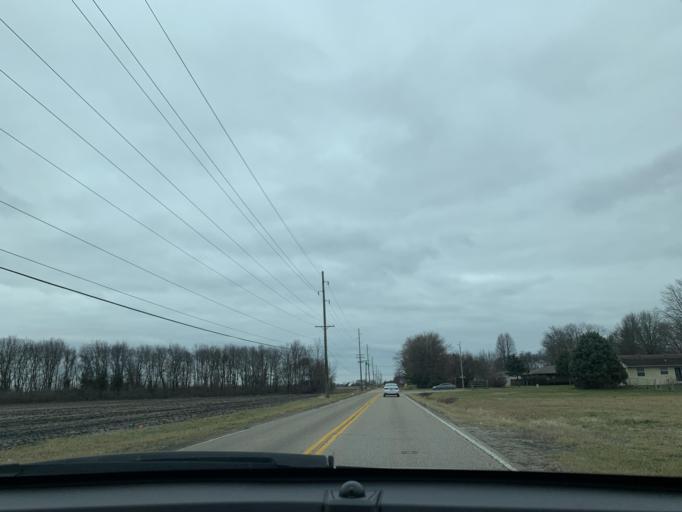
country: US
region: Illinois
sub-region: Sangamon County
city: Jerome
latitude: 39.7545
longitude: -89.6867
